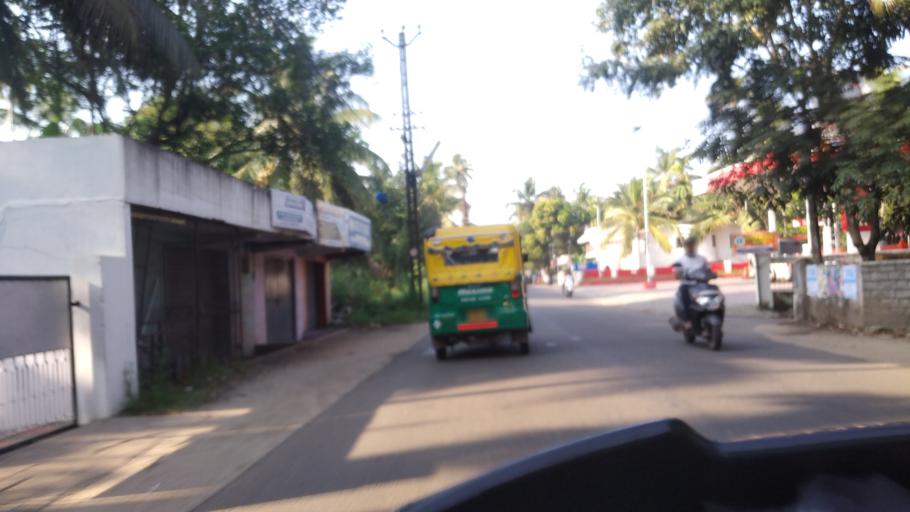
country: IN
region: Kerala
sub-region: Ernakulam
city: Elur
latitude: 10.0746
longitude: 76.2115
